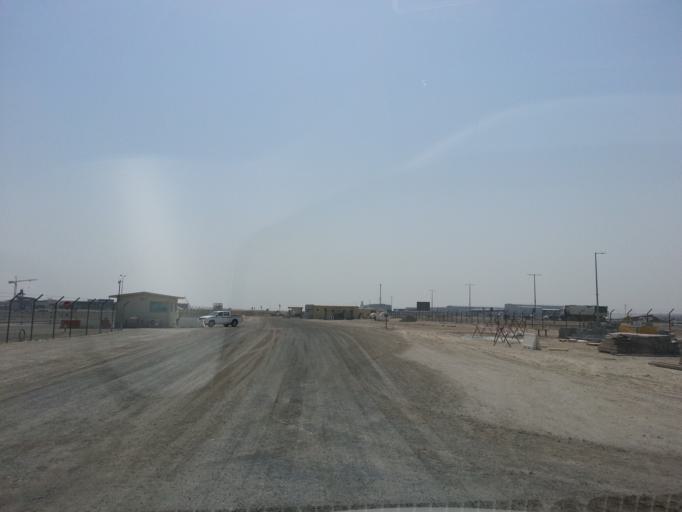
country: AE
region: Abu Dhabi
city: Abu Dhabi
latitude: 24.7798
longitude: 54.7295
